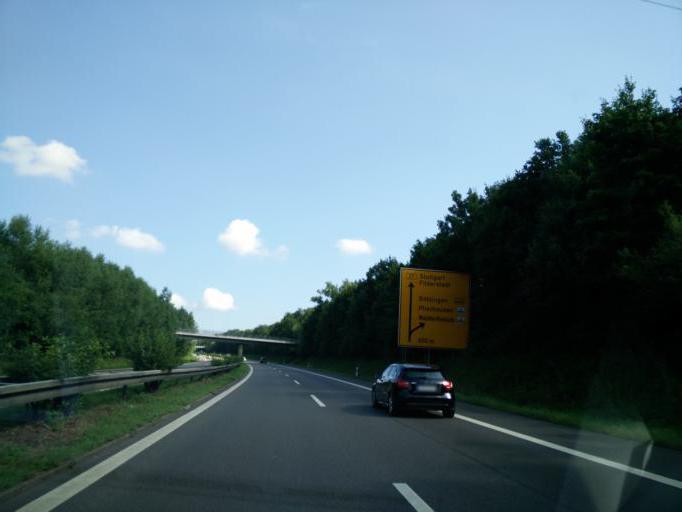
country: DE
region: Baden-Wuerttemberg
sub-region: Tuebingen Region
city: Pliezhausen
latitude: 48.5728
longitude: 9.1770
